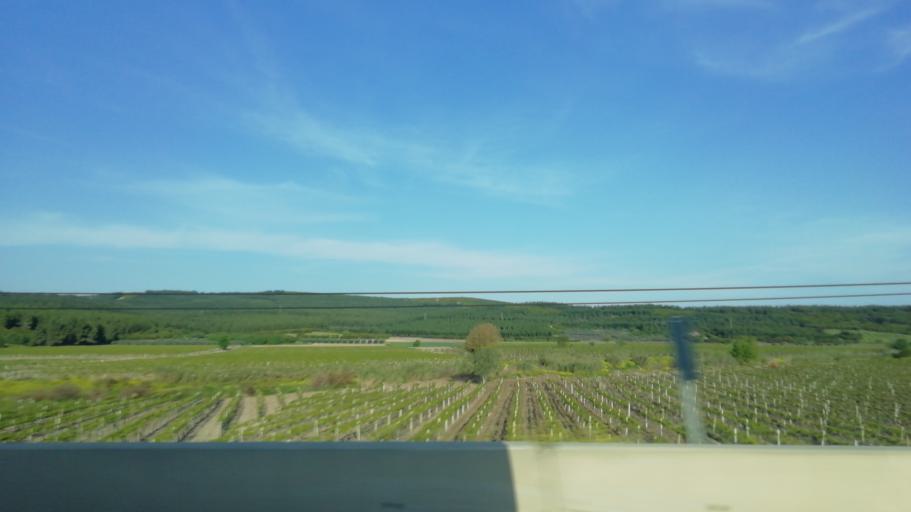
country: TR
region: Manisa
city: Halitpasa
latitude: 38.7828
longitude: 27.6700
